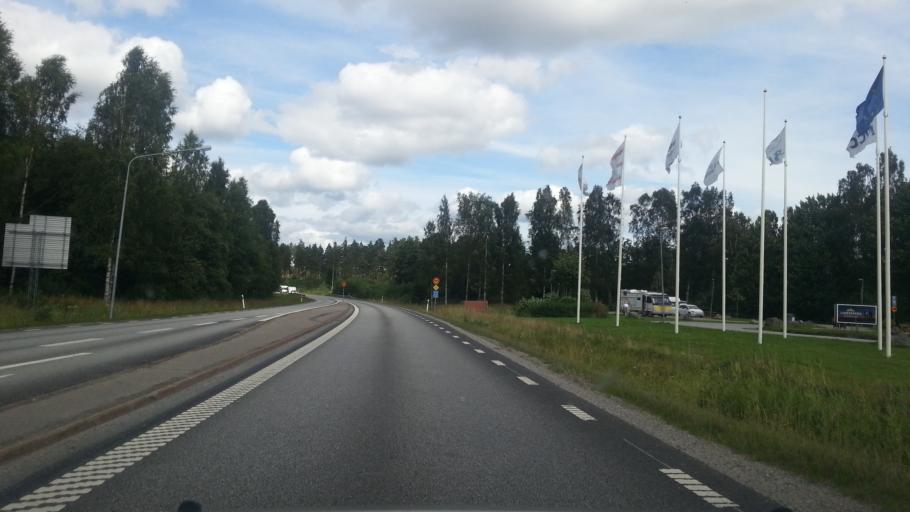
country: SE
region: OErebro
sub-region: Lindesbergs Kommun
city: Lindesberg
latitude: 59.6019
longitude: 15.1856
